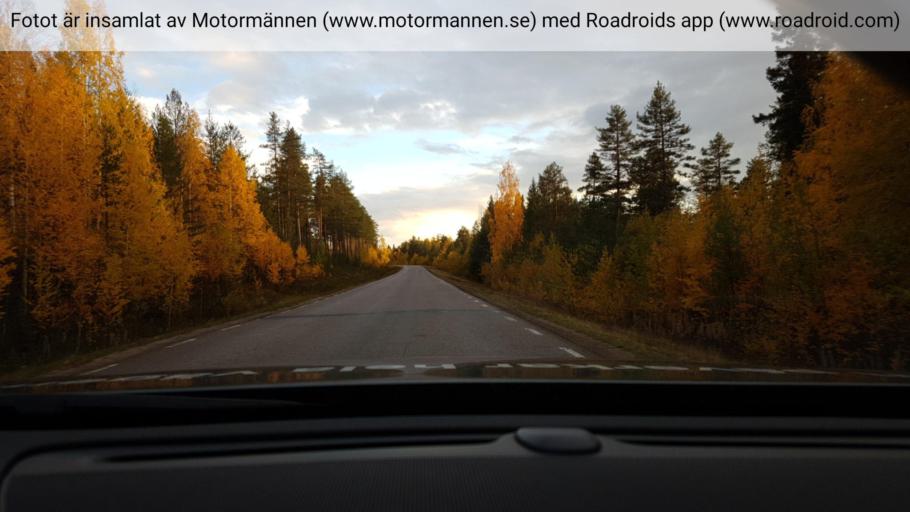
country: SE
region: Norrbotten
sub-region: Overkalix Kommun
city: OEverkalix
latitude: 66.6456
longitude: 22.7211
